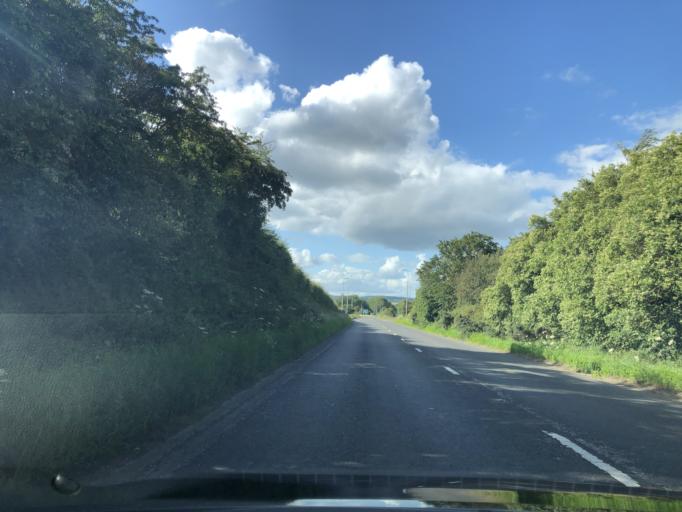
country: GB
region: Northern Ireland
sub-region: Ards District
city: Comber
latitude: 54.5562
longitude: -5.7576
